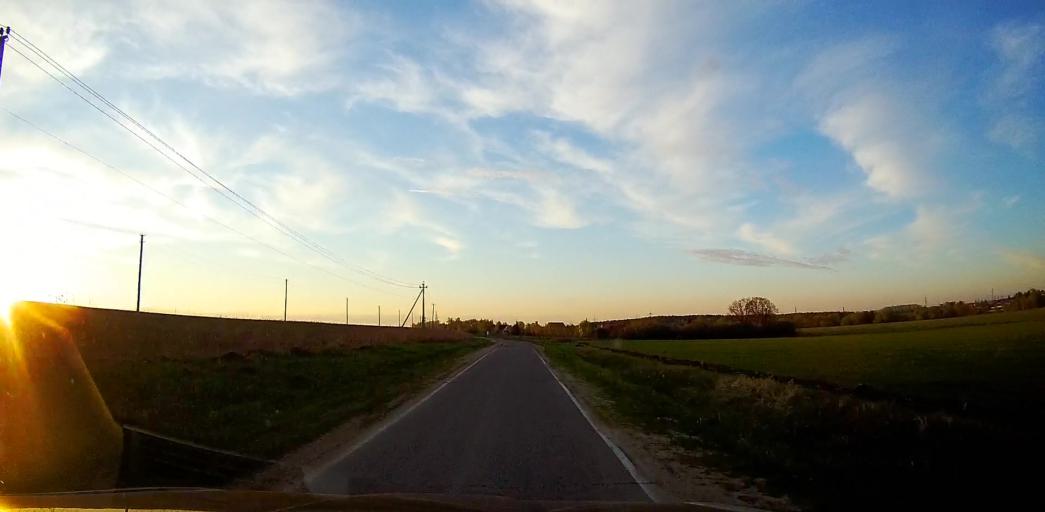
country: RU
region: Moskovskaya
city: Peski
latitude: 55.2239
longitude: 38.7360
